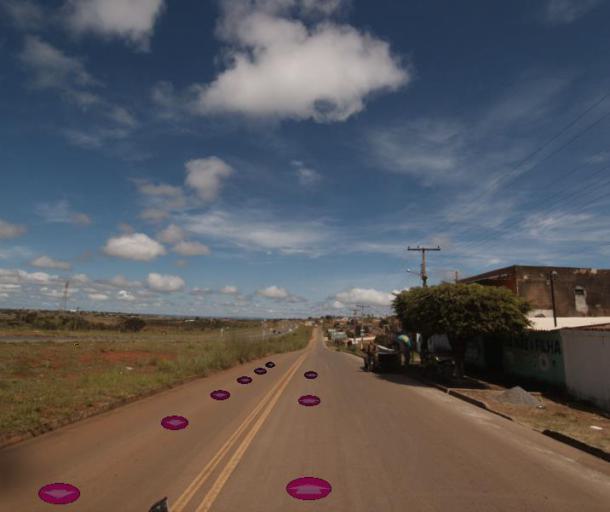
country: BR
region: Federal District
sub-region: Brasilia
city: Brasilia
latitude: -15.7395
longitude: -48.3062
